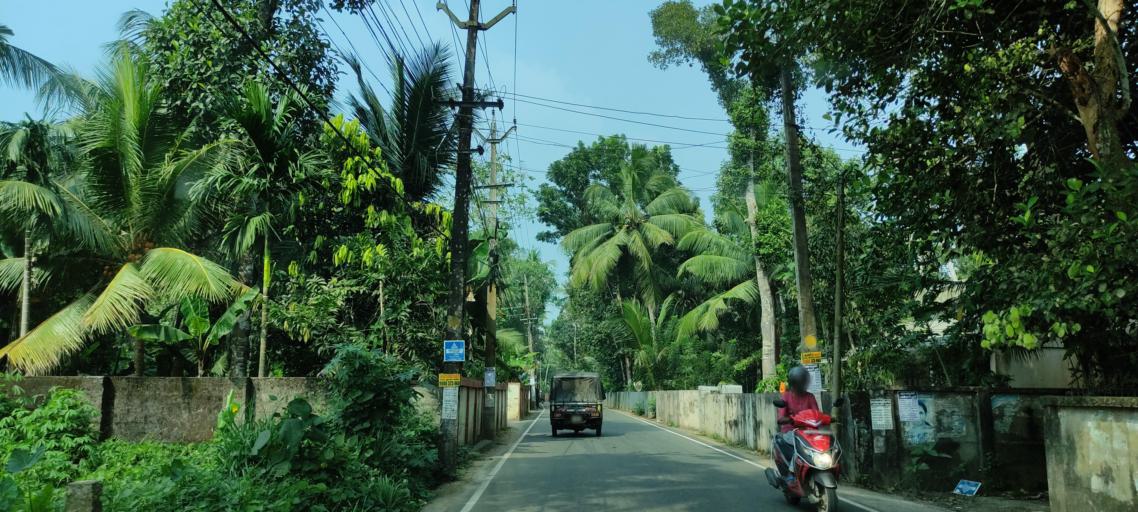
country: IN
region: Kerala
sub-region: Kottayam
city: Vaikam
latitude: 9.7429
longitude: 76.4014
